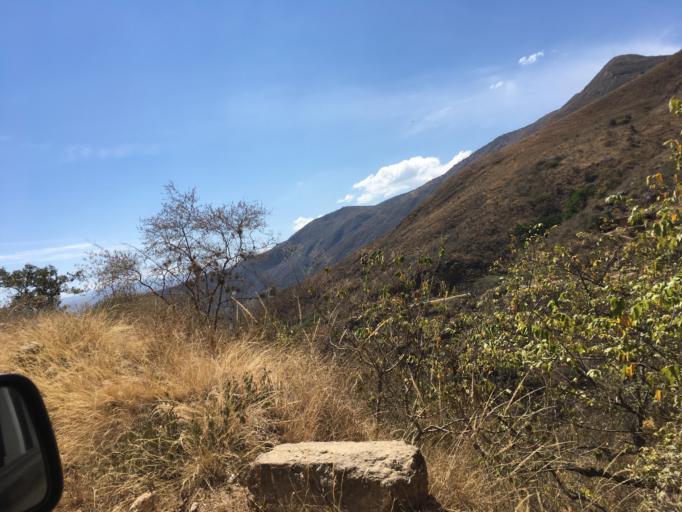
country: CO
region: Santander
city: Aratoca
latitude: 6.7933
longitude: -72.9968
